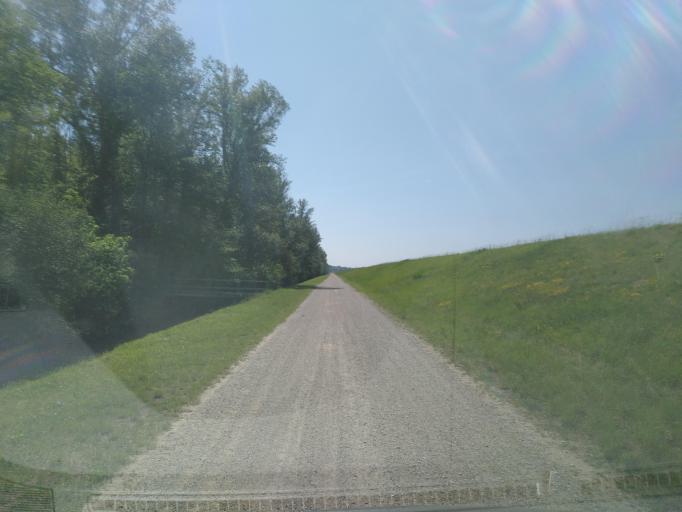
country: FR
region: Alsace
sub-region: Departement du Haut-Rhin
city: Kunheim
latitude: 48.0762
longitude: 7.5715
